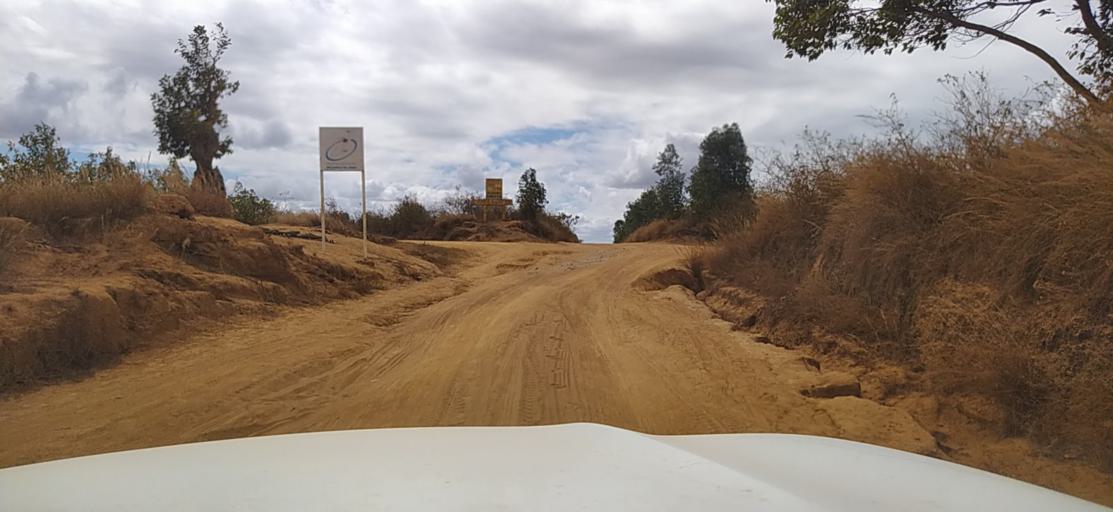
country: MG
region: Alaotra Mangoro
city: Ambatondrazaka
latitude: -17.9480
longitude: 48.2487
